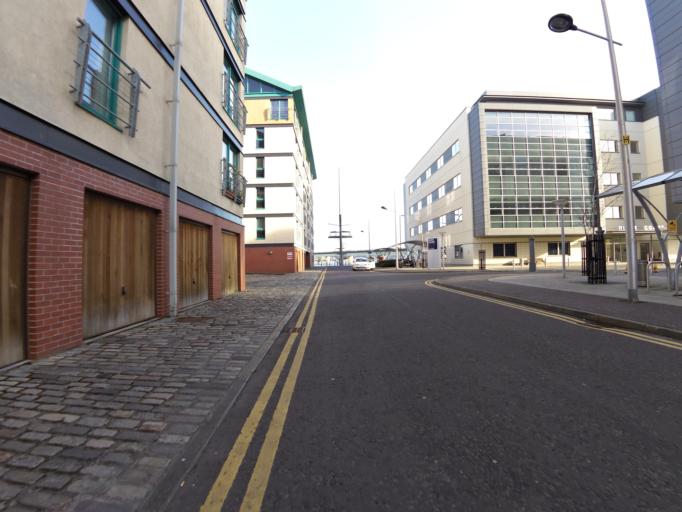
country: GB
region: Scotland
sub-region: Dundee City
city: Dundee
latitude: 56.4601
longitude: -2.9616
